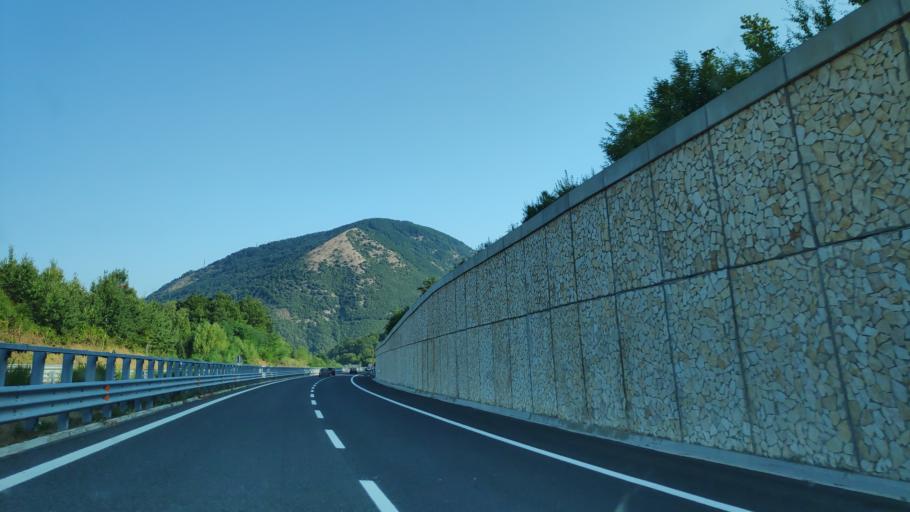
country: IT
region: Basilicate
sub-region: Provincia di Potenza
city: Lagonegro
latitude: 40.1162
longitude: 15.7851
